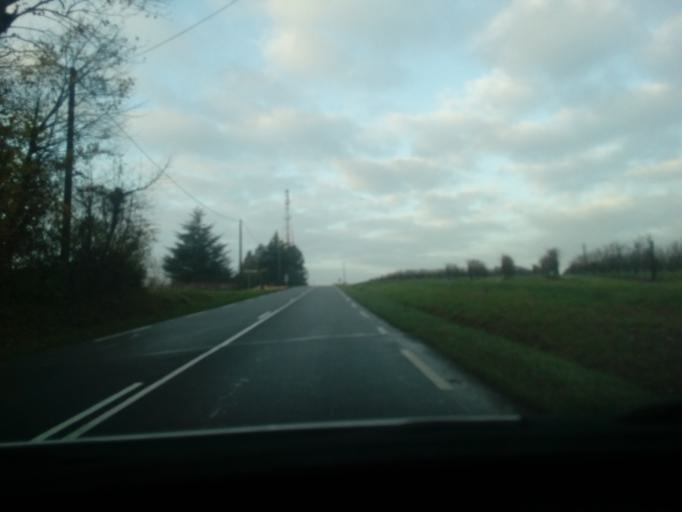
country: FR
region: Poitou-Charentes
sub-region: Departement de la Charente-Maritime
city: Jonzac
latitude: 45.4438
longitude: -0.4108
